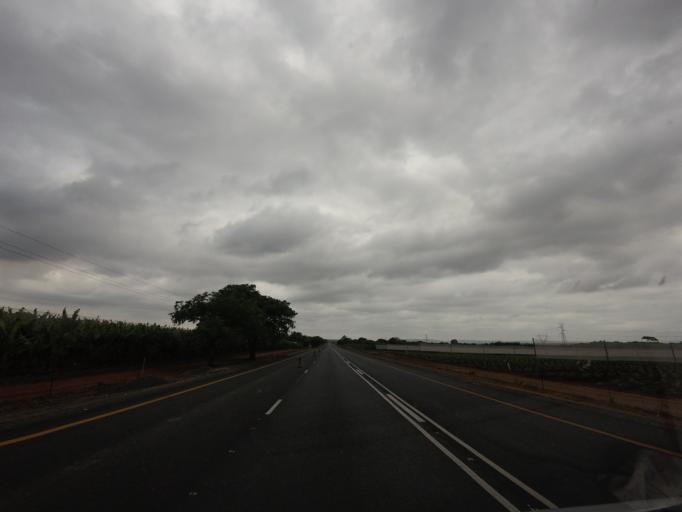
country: ZA
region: Mpumalanga
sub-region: Ehlanzeni District
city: Komatipoort
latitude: -25.4369
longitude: 31.8023
